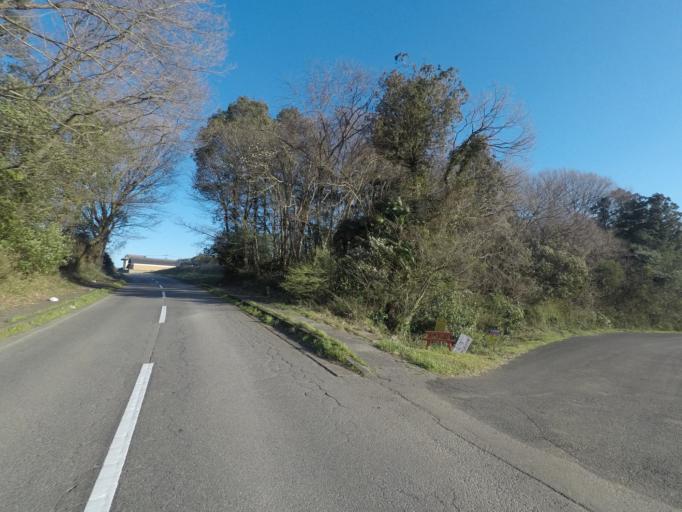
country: JP
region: Ibaraki
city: Ishige
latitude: 36.1724
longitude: 140.0155
